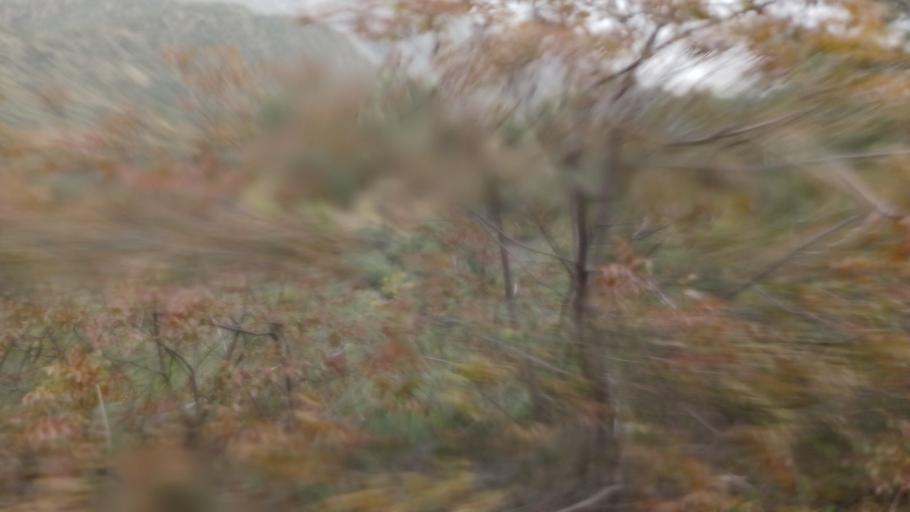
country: CY
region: Limassol
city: Parekklisha
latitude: 34.8573
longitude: 33.1086
